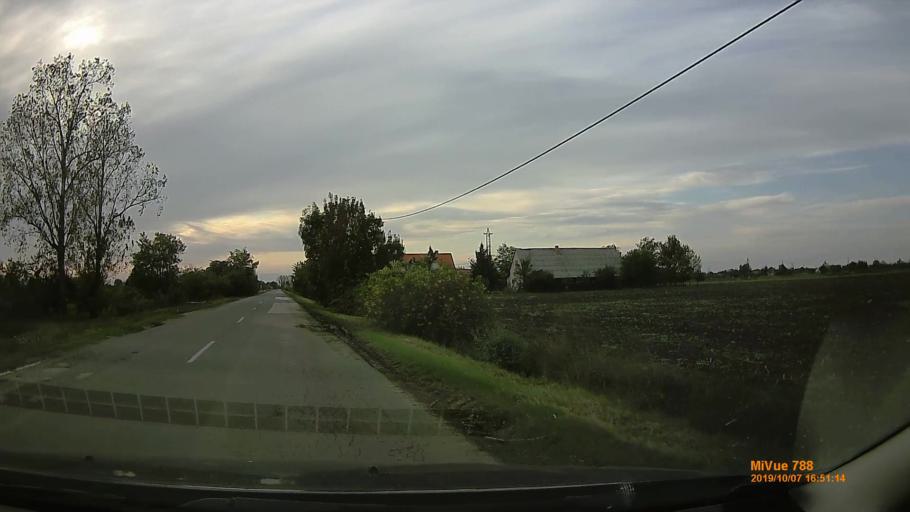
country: HU
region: Bekes
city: Szarvas
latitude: 46.8267
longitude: 20.5926
